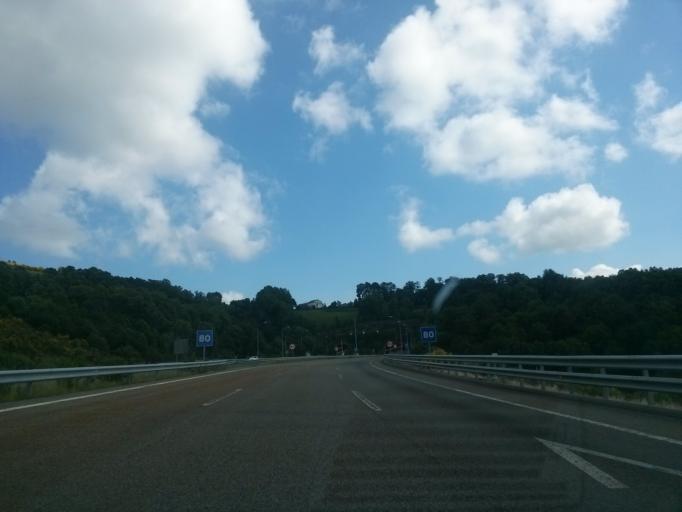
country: ES
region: Castille and Leon
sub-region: Provincia de Leon
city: Balboa
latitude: 42.7390
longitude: -7.0475
